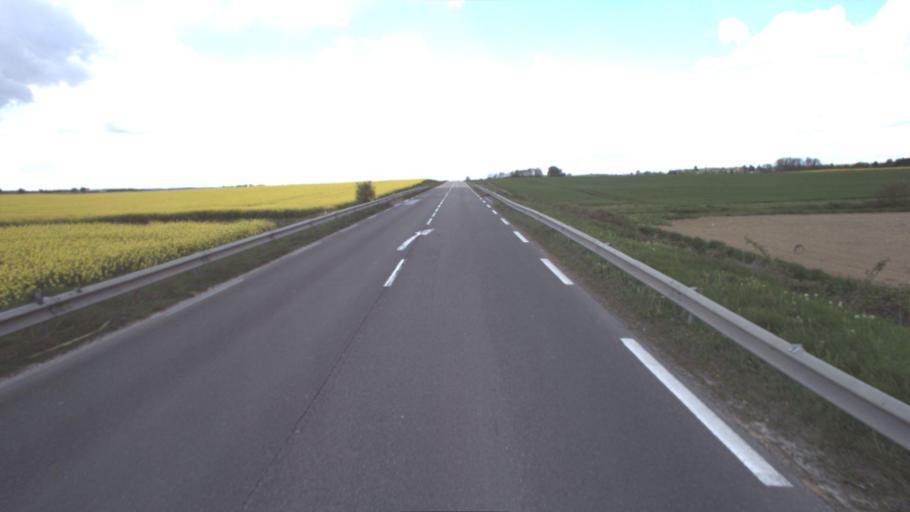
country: FR
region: Ile-de-France
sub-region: Departement de Seine-et-Marne
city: Villiers-Saint-Georges
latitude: 48.6918
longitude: 3.3725
